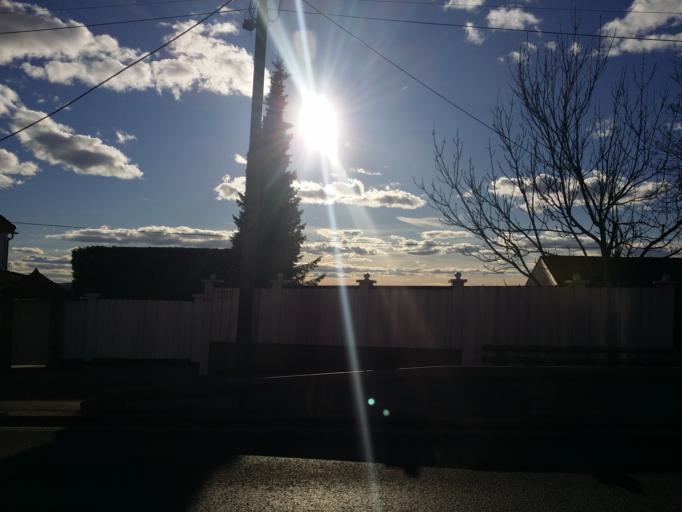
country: NO
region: Akershus
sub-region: Oppegard
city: Kolbotn
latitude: 59.8610
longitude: 10.7851
